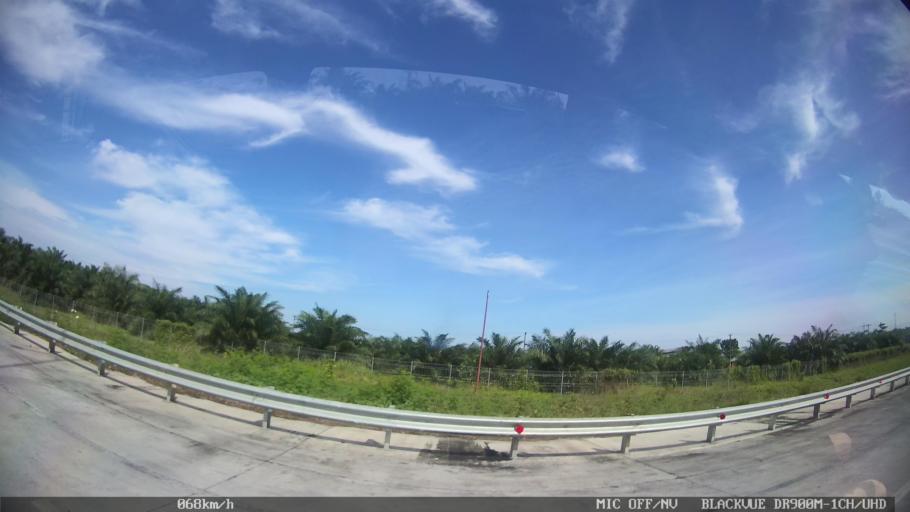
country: ID
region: North Sumatra
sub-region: Kabupaten Langkat
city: Stabat
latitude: 3.7304
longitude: 98.4901
